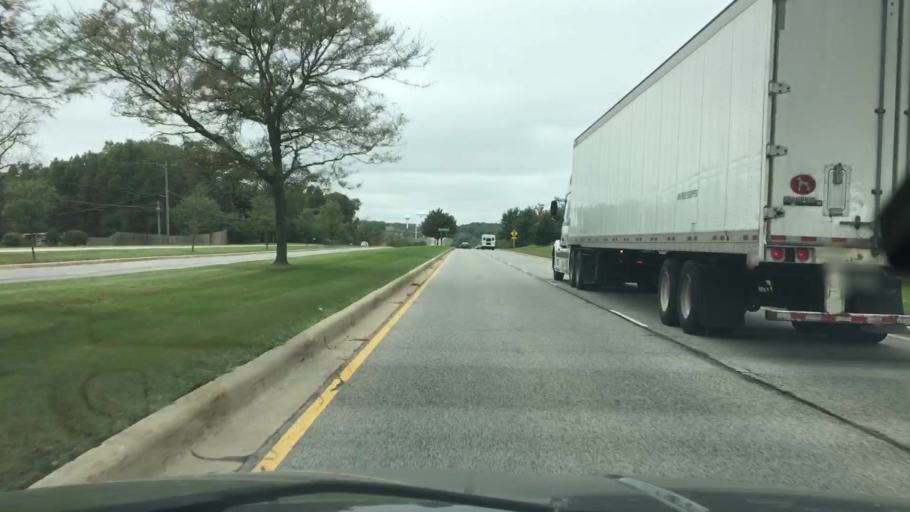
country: US
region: Illinois
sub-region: DuPage County
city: Woodridge
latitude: 41.7501
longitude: -88.0574
